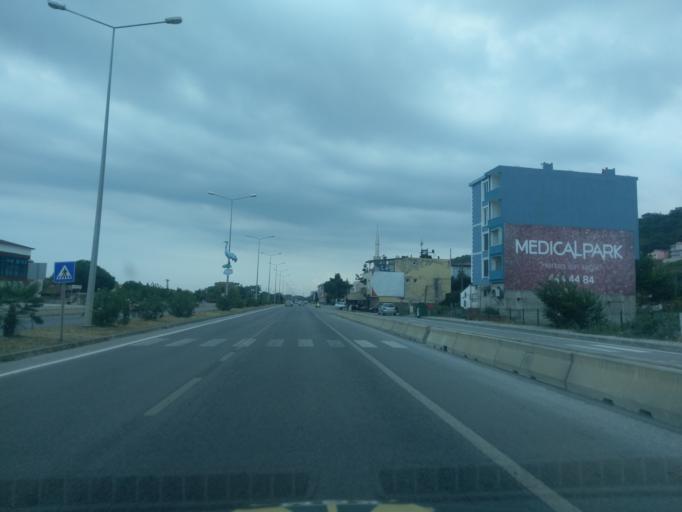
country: TR
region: Samsun
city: Taflan
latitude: 41.3875
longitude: 36.2057
